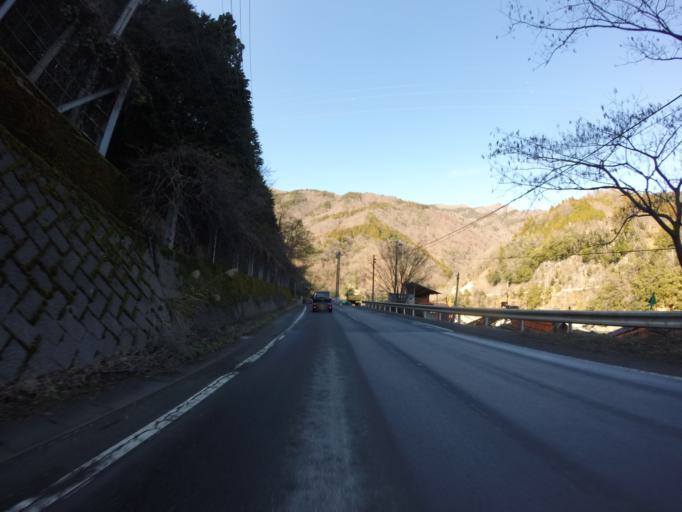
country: JP
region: Yamanashi
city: Ryuo
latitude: 35.4222
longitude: 138.3889
